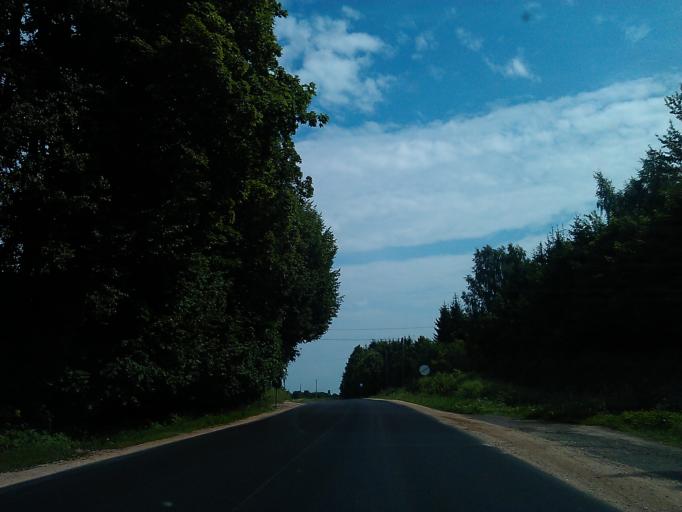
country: LV
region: Cesu Rajons
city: Cesis
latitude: 57.3285
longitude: 25.3116
